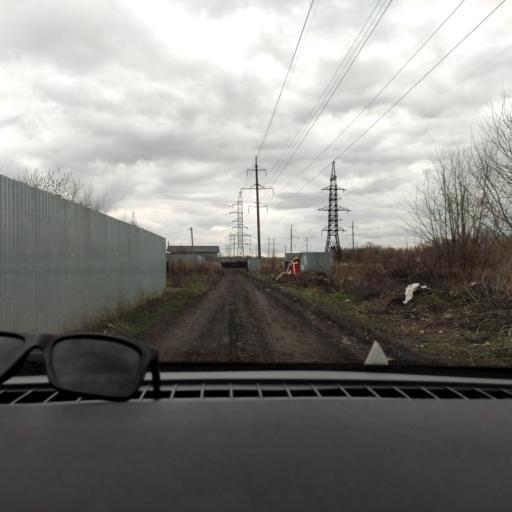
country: RU
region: Samara
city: Dubovyy Umet
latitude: 53.0928
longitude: 50.2339
